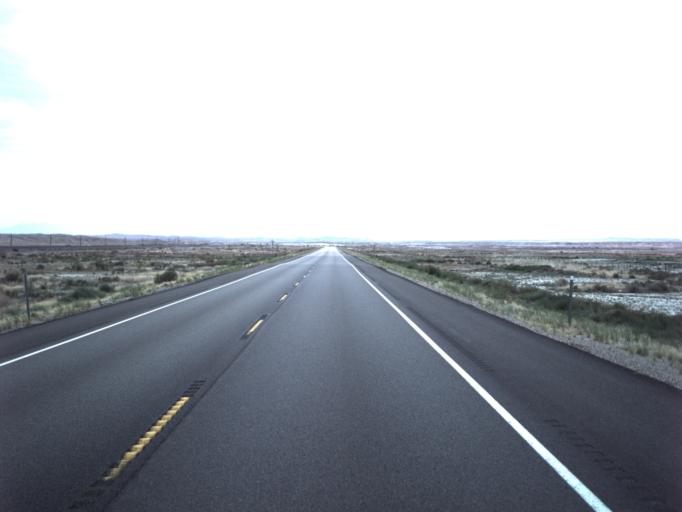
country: US
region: Utah
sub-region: Carbon County
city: East Carbon City
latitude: 39.0118
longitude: -110.2835
